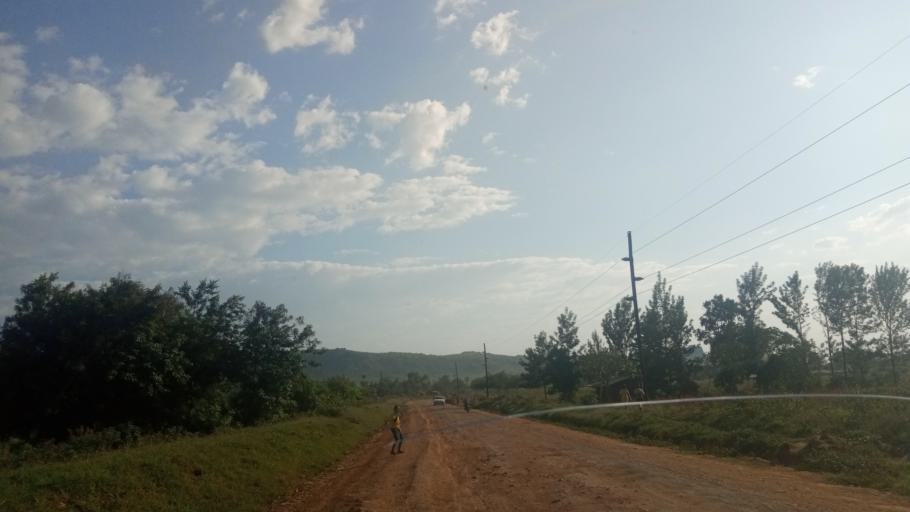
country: UG
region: Eastern Region
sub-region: Kapchorwa District
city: Kapchorwa
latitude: 1.4110
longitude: 34.3482
